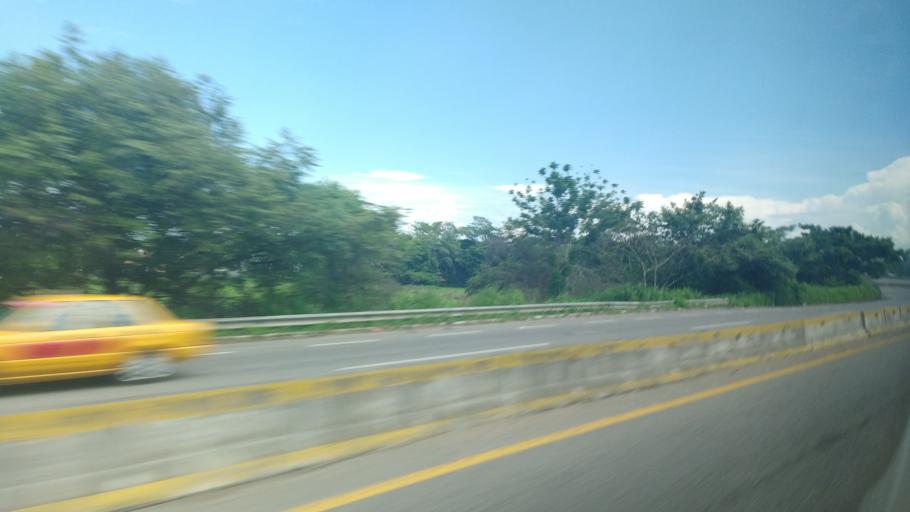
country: MX
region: Tabasco
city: Parrilla
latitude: 17.9129
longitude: -92.9235
